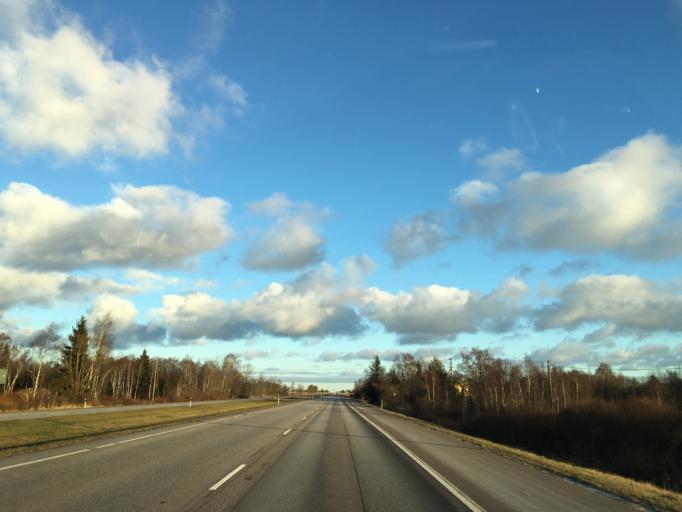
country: EE
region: Harju
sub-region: Saue linn
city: Saue
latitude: 59.2918
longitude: 24.5442
